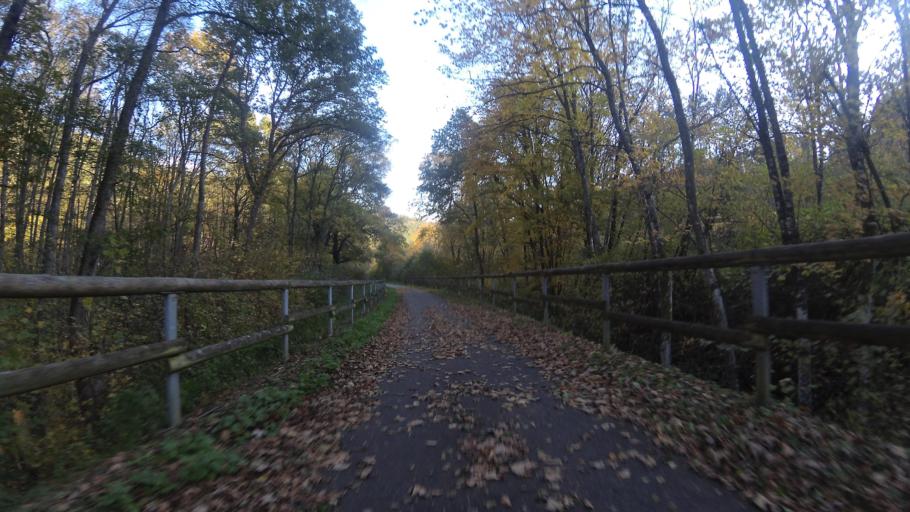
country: DE
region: Rheinland-Pfalz
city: Gusterath
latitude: 49.6908
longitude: 6.7259
